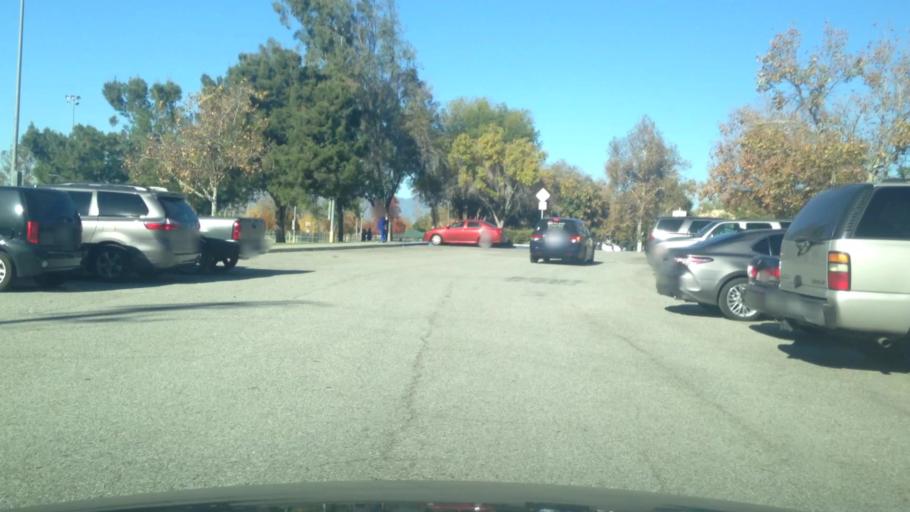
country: US
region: California
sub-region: Riverside County
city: Highgrove
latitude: 34.0105
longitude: -117.3536
